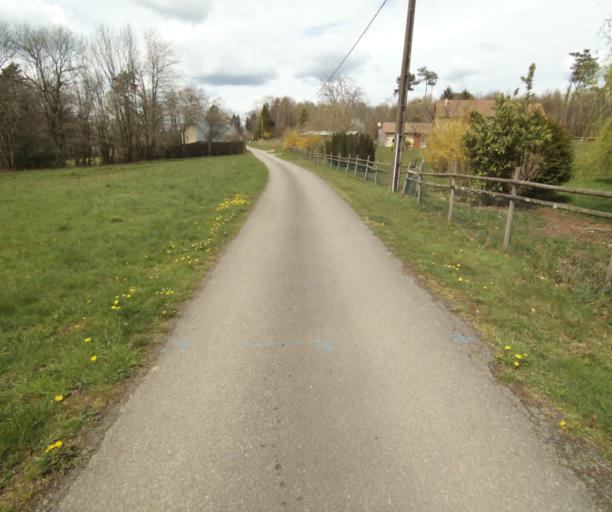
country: FR
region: Limousin
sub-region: Departement de la Correze
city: Laguenne
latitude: 45.2213
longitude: 1.8859
